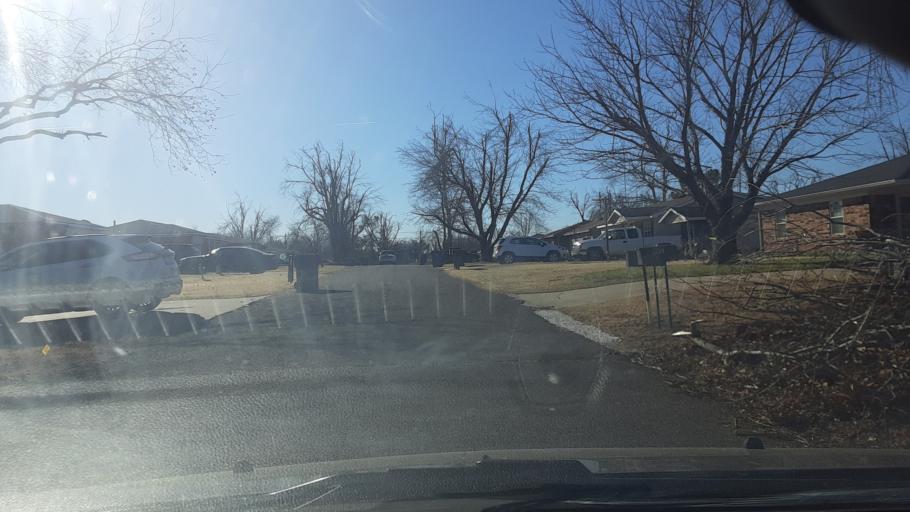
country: US
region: Oklahoma
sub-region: Logan County
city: Guthrie
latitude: 35.8580
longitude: -97.4325
